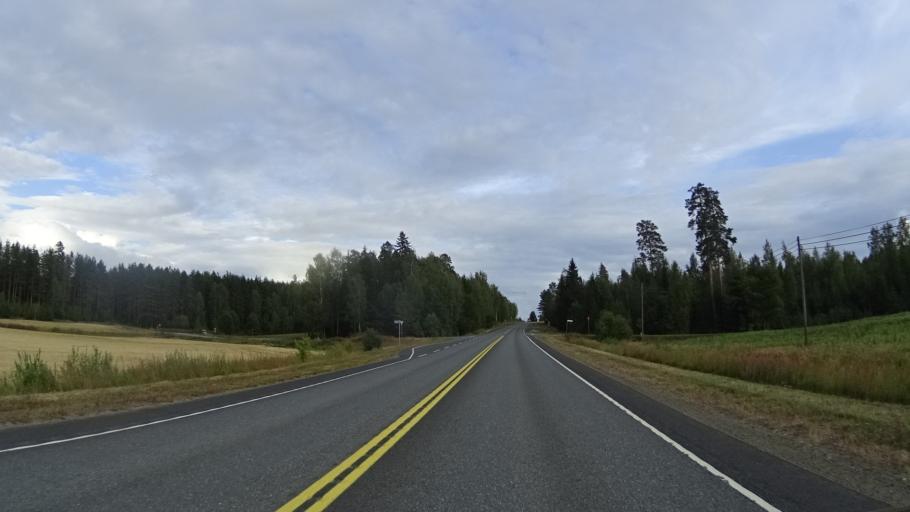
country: FI
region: Haeme
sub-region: Haemeenlinna
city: Parola
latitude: 61.0360
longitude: 24.2636
